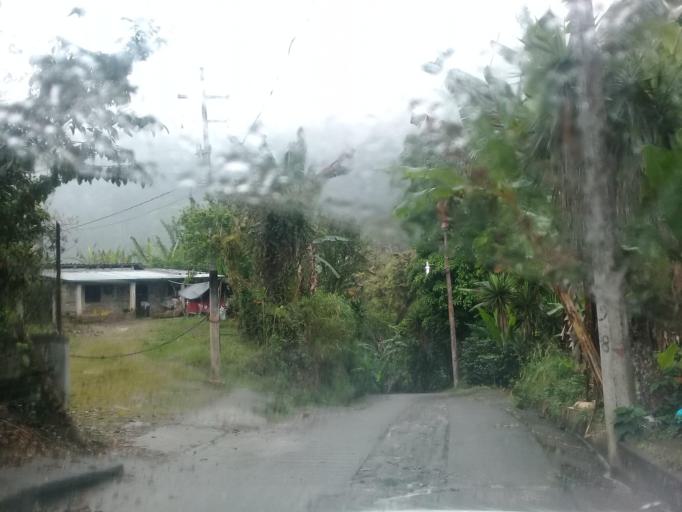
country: MX
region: Veracruz
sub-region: Amatlan de los Reyes
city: Centro de Readaptacion Social
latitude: 18.8006
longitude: -96.9515
